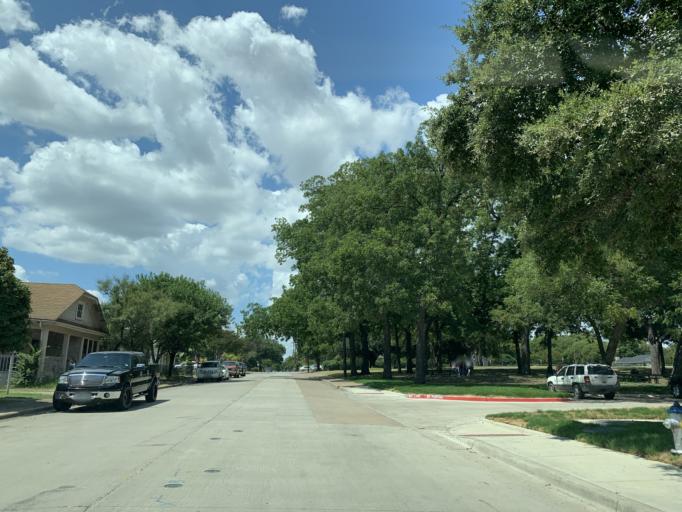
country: US
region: Texas
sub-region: Dallas County
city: Dallas
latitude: 32.7524
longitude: -96.8359
